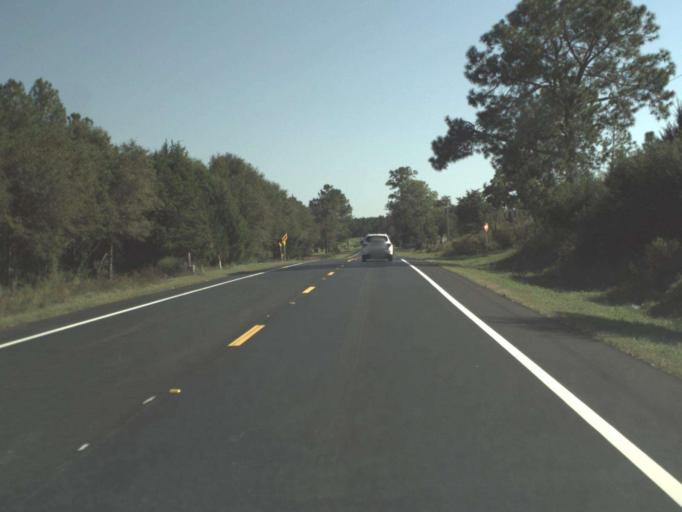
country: US
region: Florida
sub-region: Walton County
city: DeFuniak Springs
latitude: 30.8322
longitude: -86.2324
